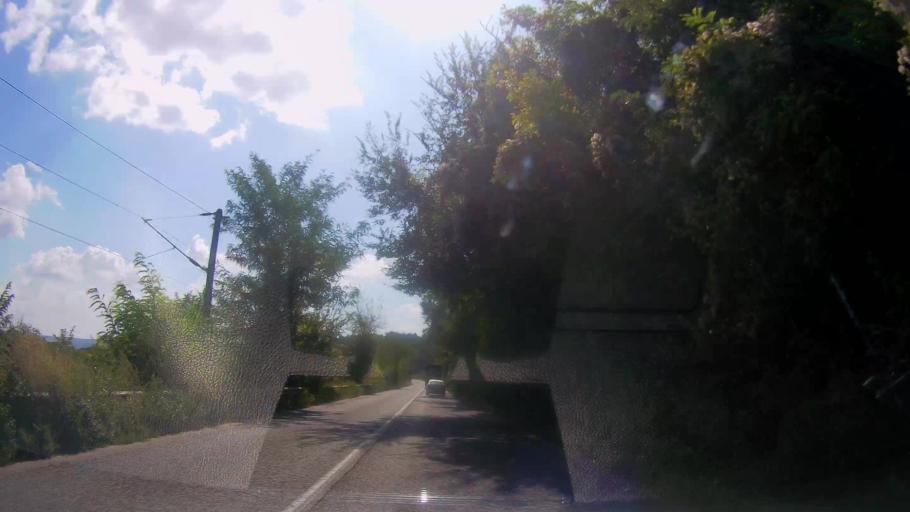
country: BG
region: Veliko Turnovo
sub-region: Obshtina Polski Trumbesh
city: Polski Trumbesh
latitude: 43.4360
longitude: 25.6548
